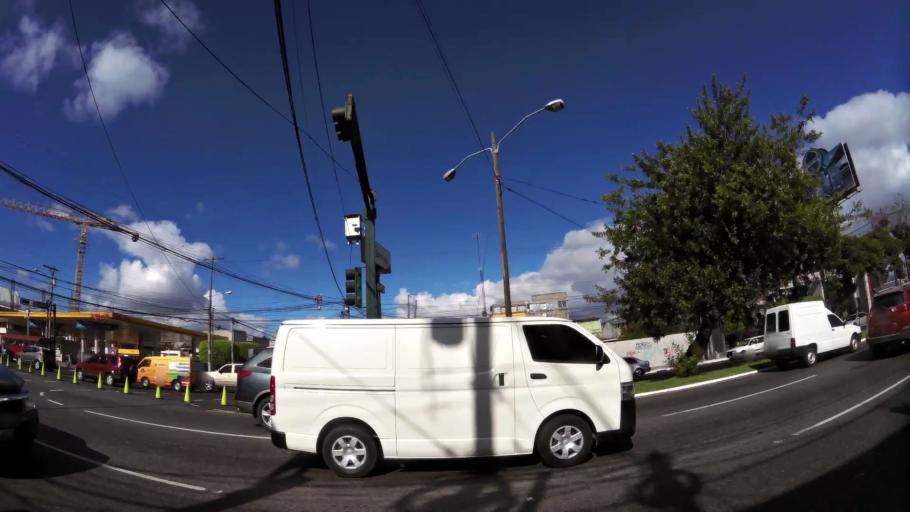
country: GT
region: Guatemala
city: Guatemala City
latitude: 14.6216
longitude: -90.5493
